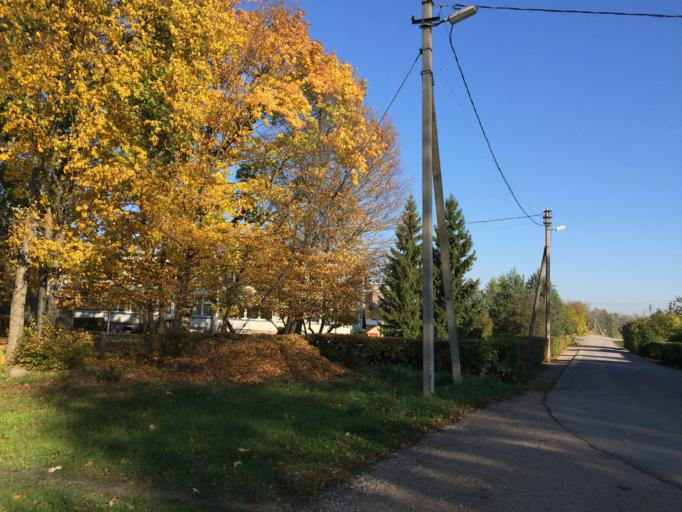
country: LT
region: Klaipedos apskritis
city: Kretinga
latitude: 55.8995
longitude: 21.2522
